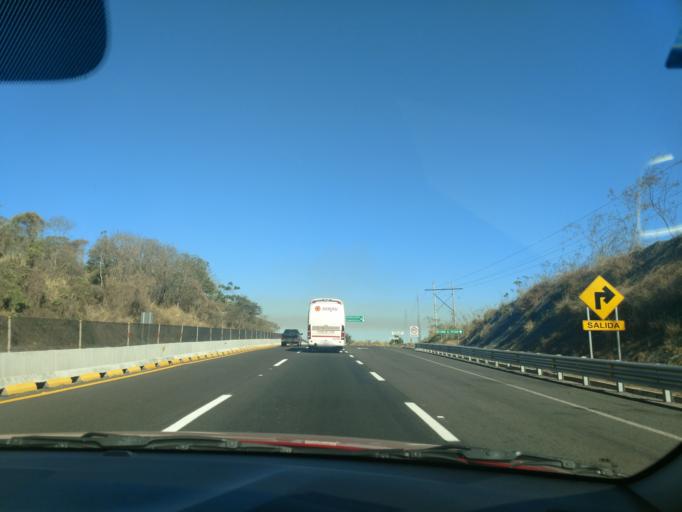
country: MX
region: Nayarit
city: Tepic
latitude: 21.5594
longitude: -104.9662
